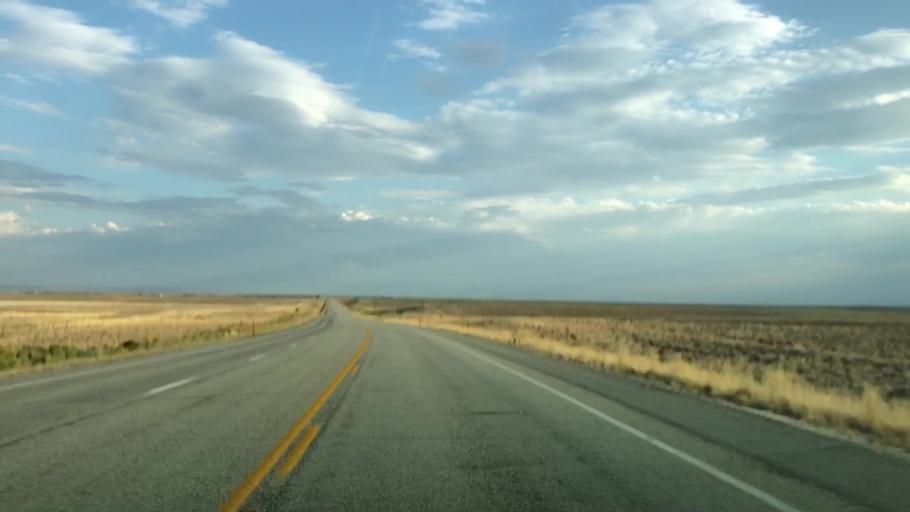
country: US
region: Wyoming
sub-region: Sweetwater County
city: North Rock Springs
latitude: 42.1893
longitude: -109.4803
